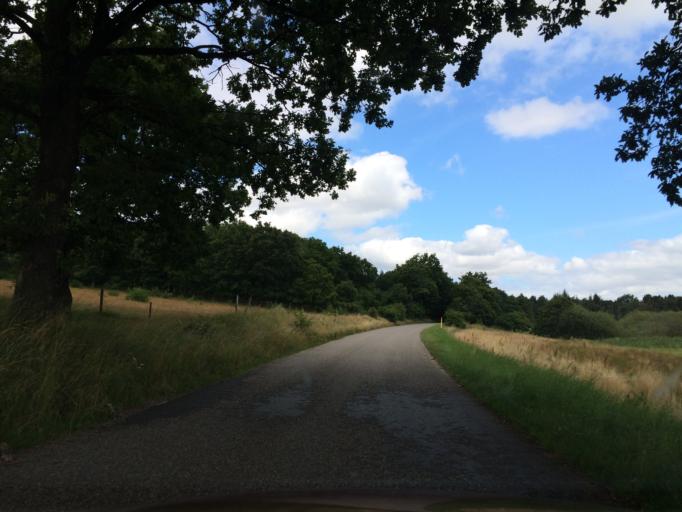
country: DK
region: Central Jutland
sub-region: Silkeborg Kommune
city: Svejbaek
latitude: 56.2007
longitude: 9.6462
